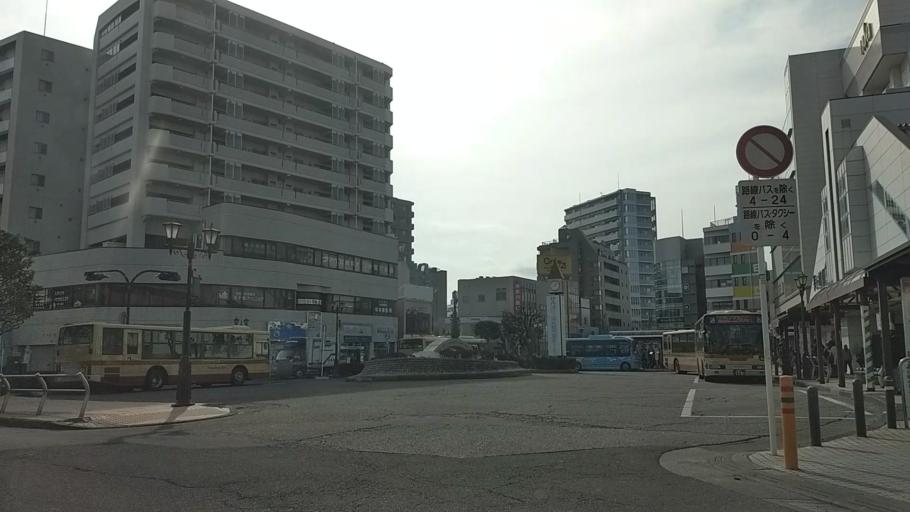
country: JP
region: Kanagawa
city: Chigasaki
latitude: 35.3302
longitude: 139.4074
